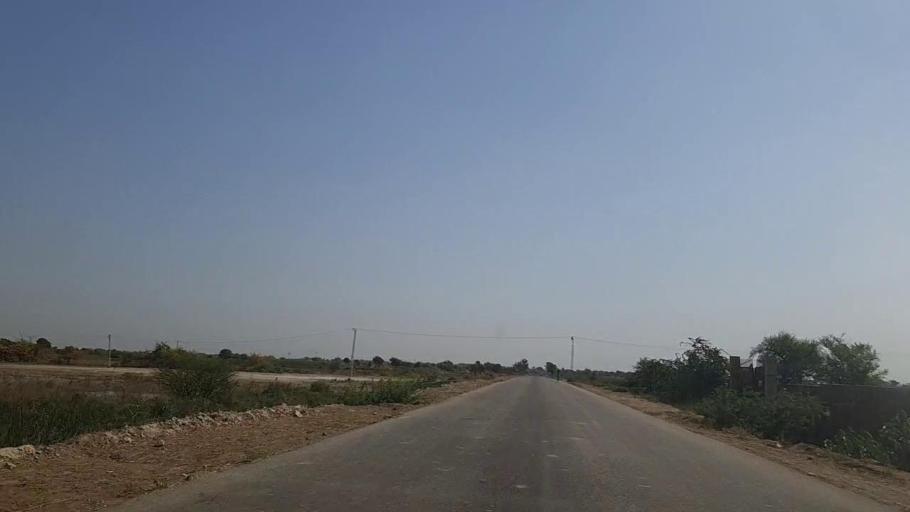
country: PK
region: Sindh
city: Daro Mehar
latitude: 24.7711
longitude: 68.2096
